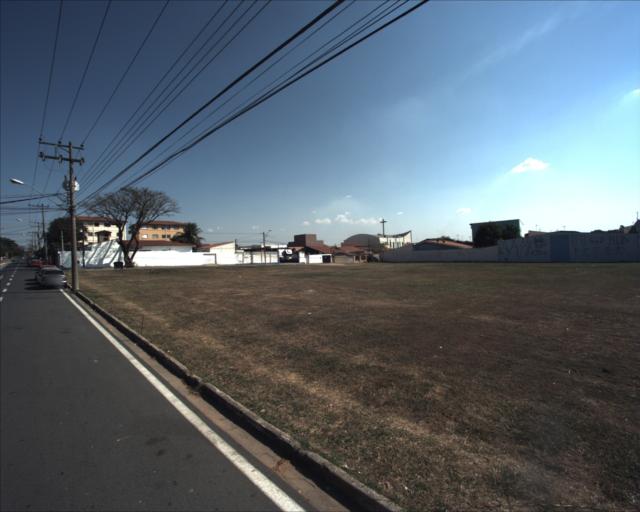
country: BR
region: Sao Paulo
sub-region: Sorocaba
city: Sorocaba
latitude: -23.4704
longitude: -47.4429
